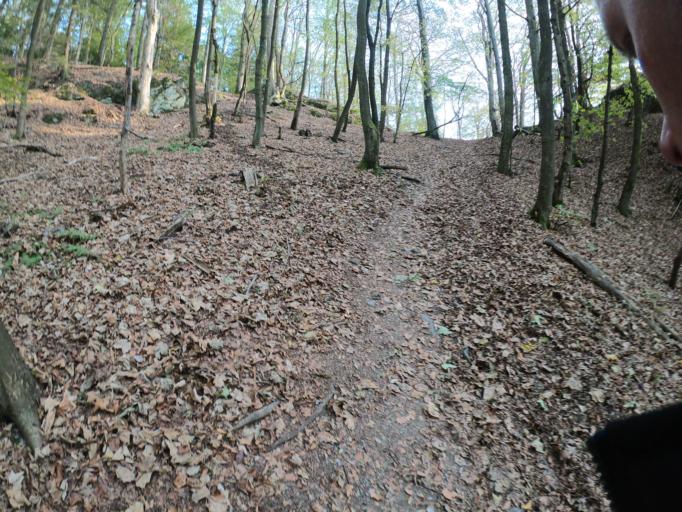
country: DE
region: Hesse
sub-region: Regierungsbezirk Darmstadt
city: Glashutten
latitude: 50.2300
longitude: 8.4241
